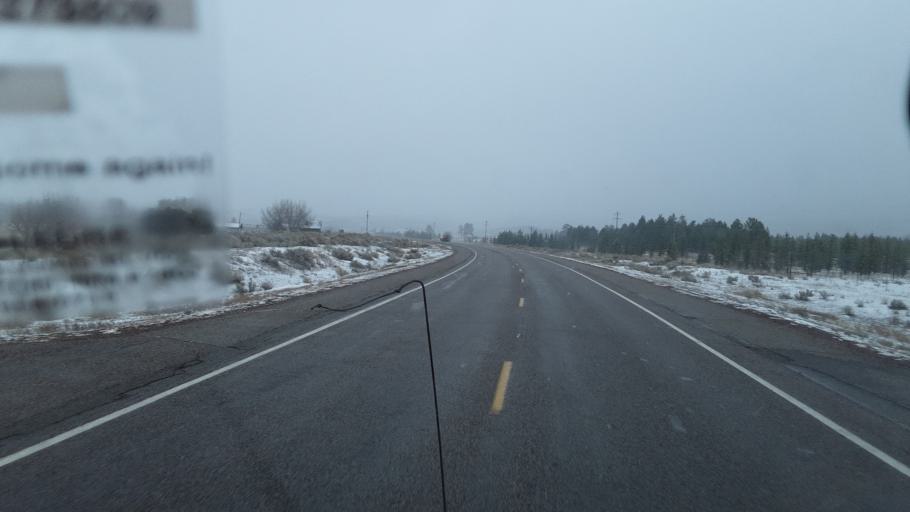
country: US
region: New Mexico
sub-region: Rio Arriba County
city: Tierra Amarilla
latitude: 36.7600
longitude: -106.5579
